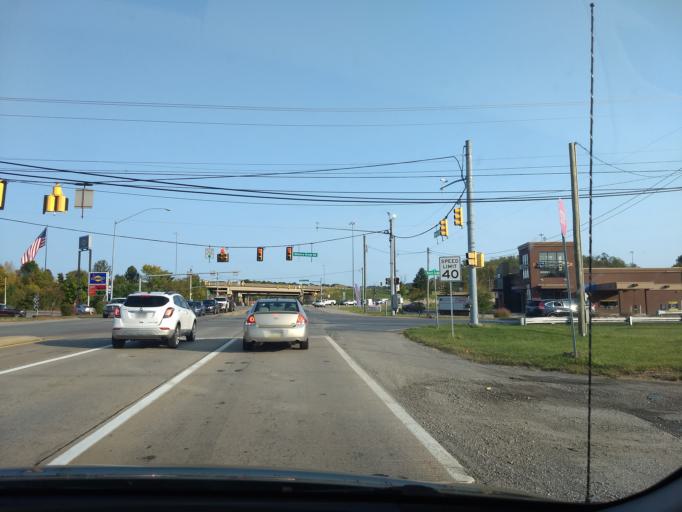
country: US
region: Pennsylvania
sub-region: Allegheny County
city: Bridgeville
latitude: 40.3572
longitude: -80.1208
